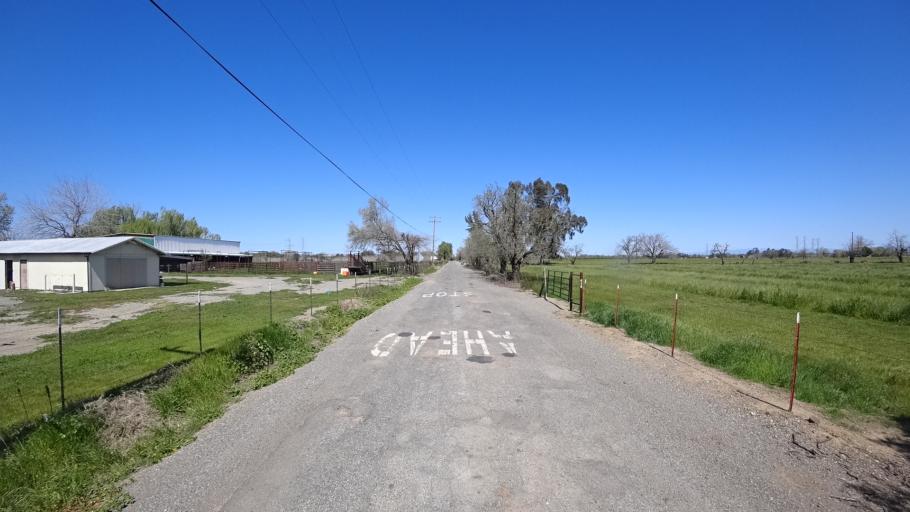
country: US
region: California
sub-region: Glenn County
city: Orland
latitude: 39.7759
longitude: -122.2712
